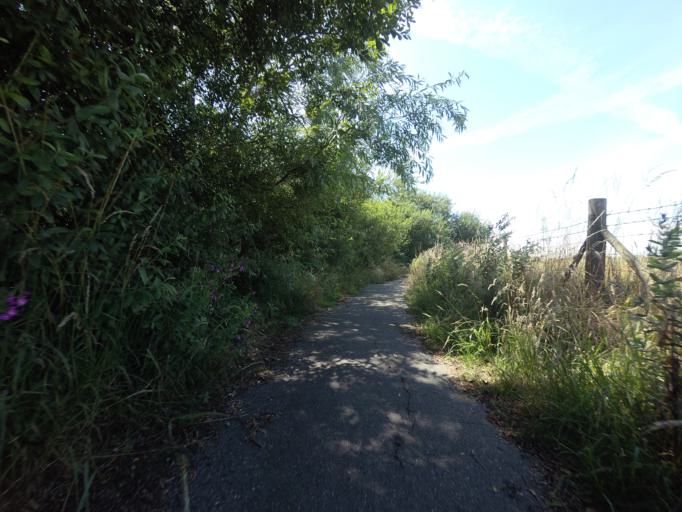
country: GB
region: England
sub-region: Kent
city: Lydd
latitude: 50.9460
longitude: 0.8935
